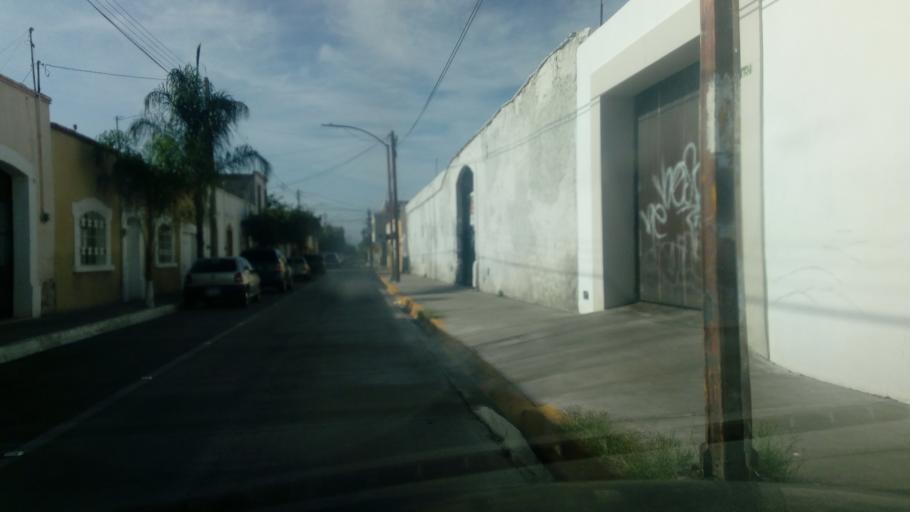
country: MX
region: Durango
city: Victoria de Durango
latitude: 24.0337
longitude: -104.6704
